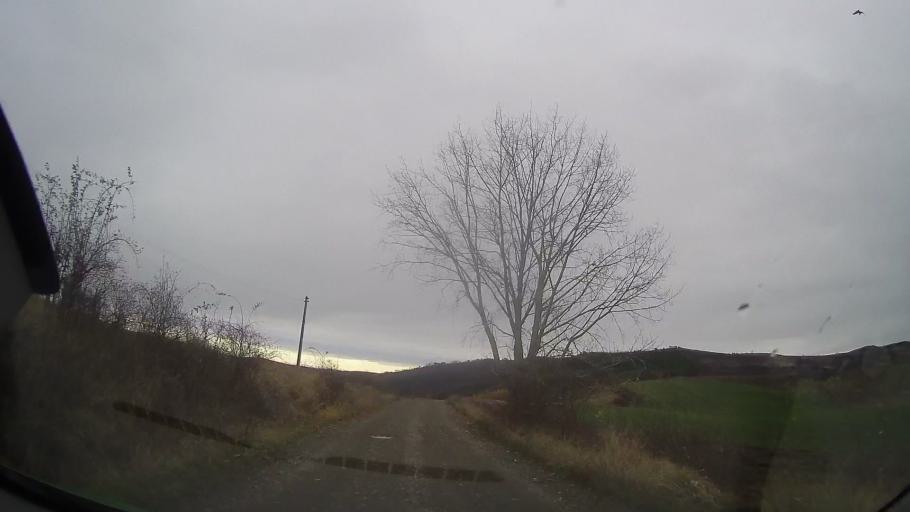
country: RO
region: Mures
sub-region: Comuna Bala
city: Bala
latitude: 46.6744
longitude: 24.4840
